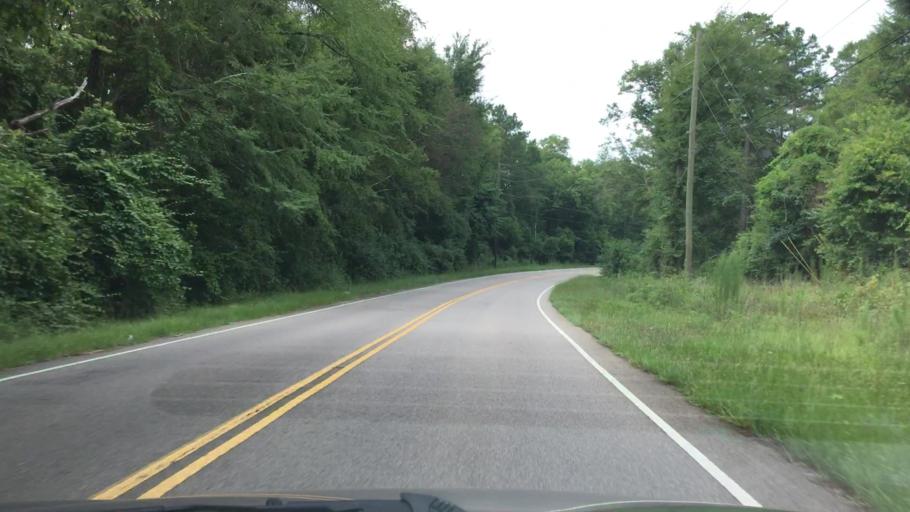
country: US
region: South Carolina
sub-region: Aiken County
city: Belvedere
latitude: 33.5644
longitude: -81.9399
